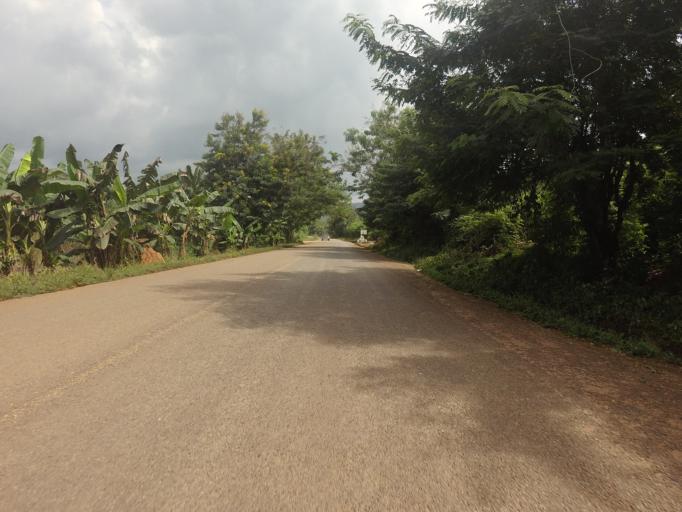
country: GH
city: Akropong
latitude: 5.9567
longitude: -0.1733
